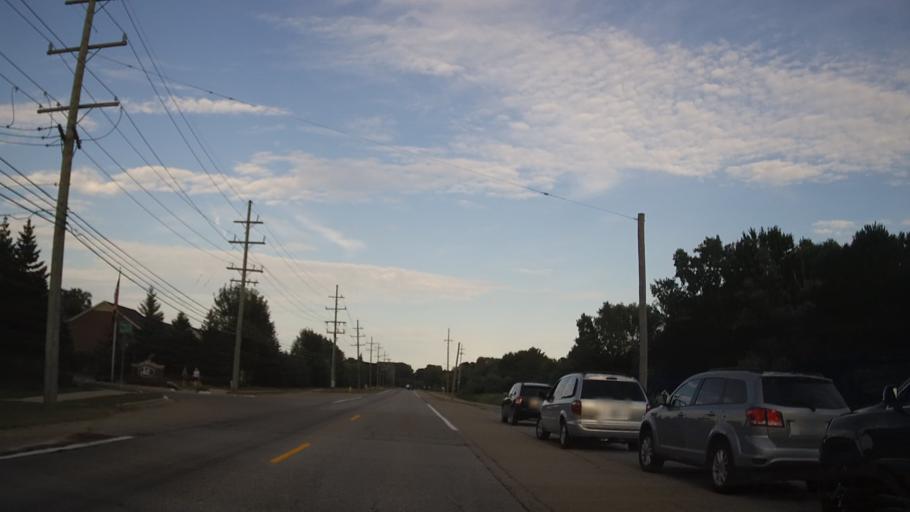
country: US
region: Michigan
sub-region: Macomb County
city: Clinton
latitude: 42.5989
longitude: -82.9271
